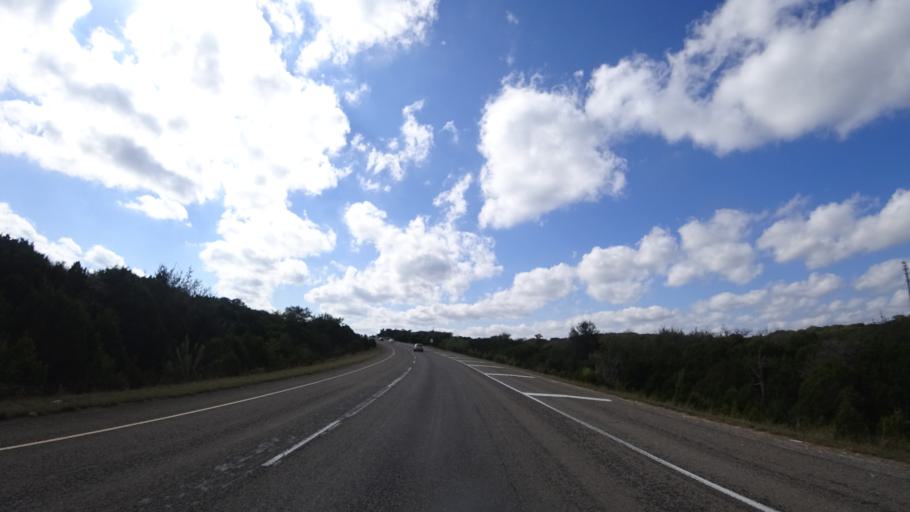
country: US
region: Texas
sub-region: Travis County
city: Barton Creek
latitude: 30.2799
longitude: -97.9091
